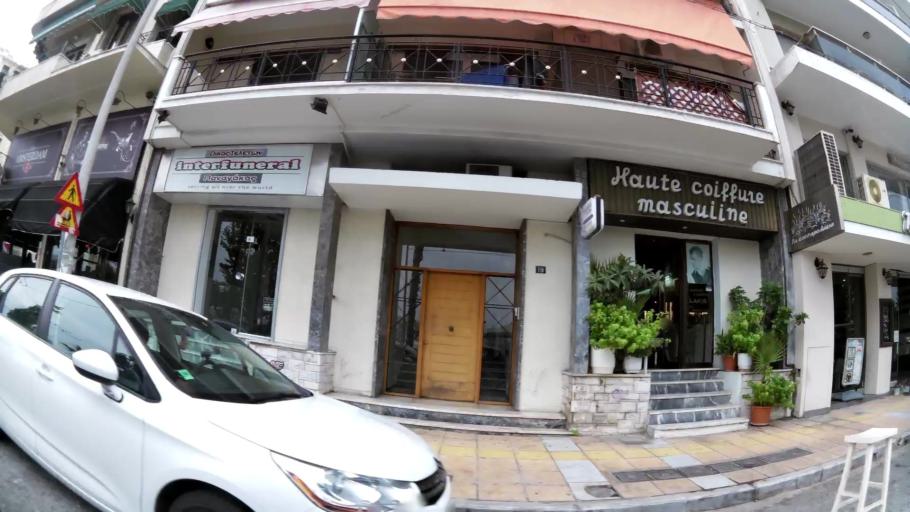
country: GR
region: Attica
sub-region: Nomos Attikis
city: Piraeus
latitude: 37.9367
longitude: 23.6507
